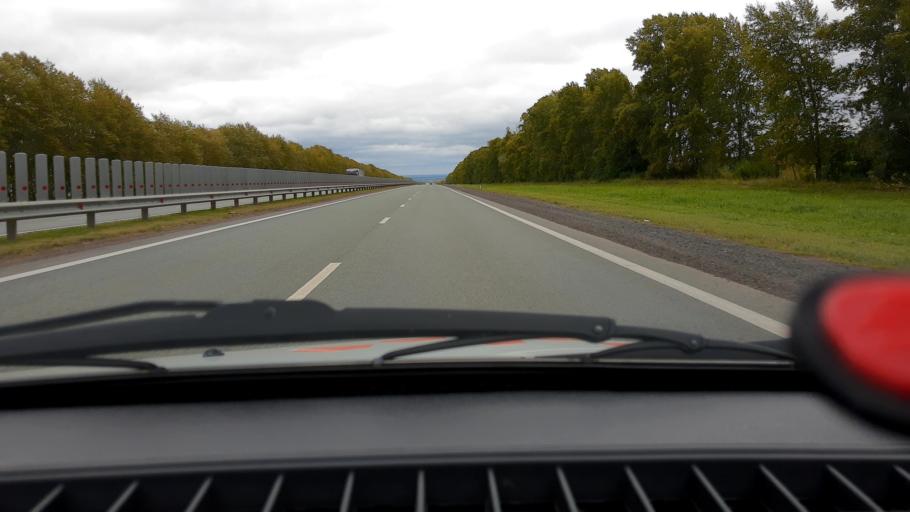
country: RU
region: Bashkortostan
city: Kushnarenkovo
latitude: 55.0431
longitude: 55.4491
